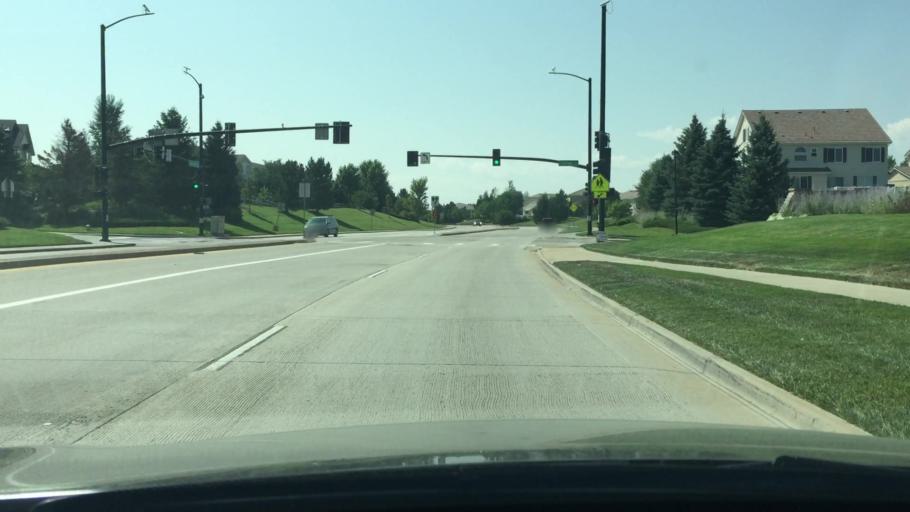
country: US
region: Colorado
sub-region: Arapahoe County
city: Dove Valley
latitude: 39.6028
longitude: -104.7871
